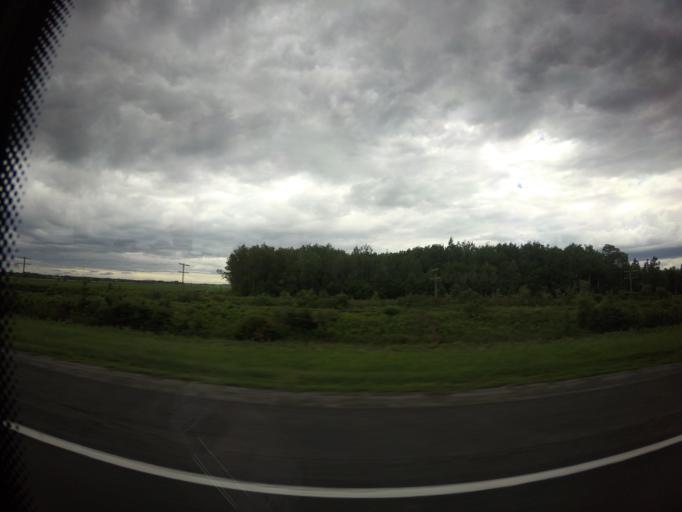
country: CA
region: Quebec
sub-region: Chaudiere-Appalaches
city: Saint-Antoine-de-Tilly
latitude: 46.5255
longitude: -71.6445
